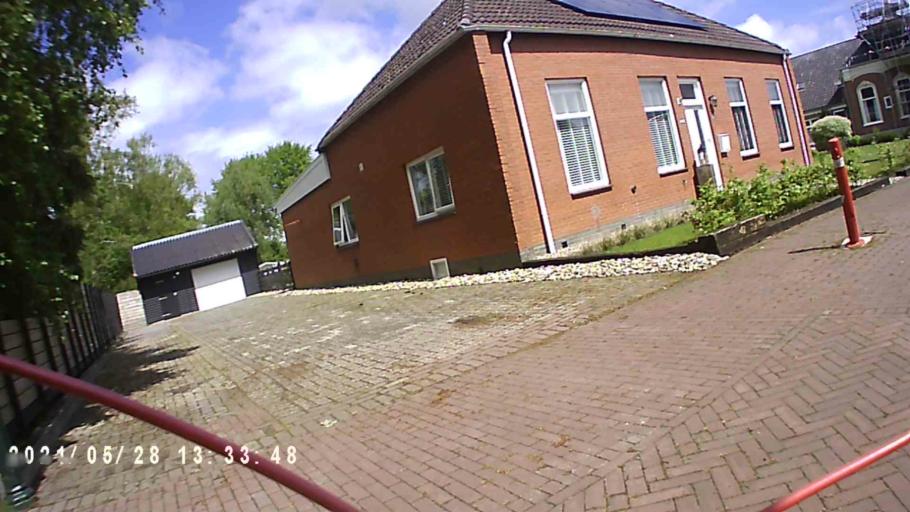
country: NL
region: Groningen
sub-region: Gemeente  Oldambt
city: Winschoten
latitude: 53.2038
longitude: 7.0429
